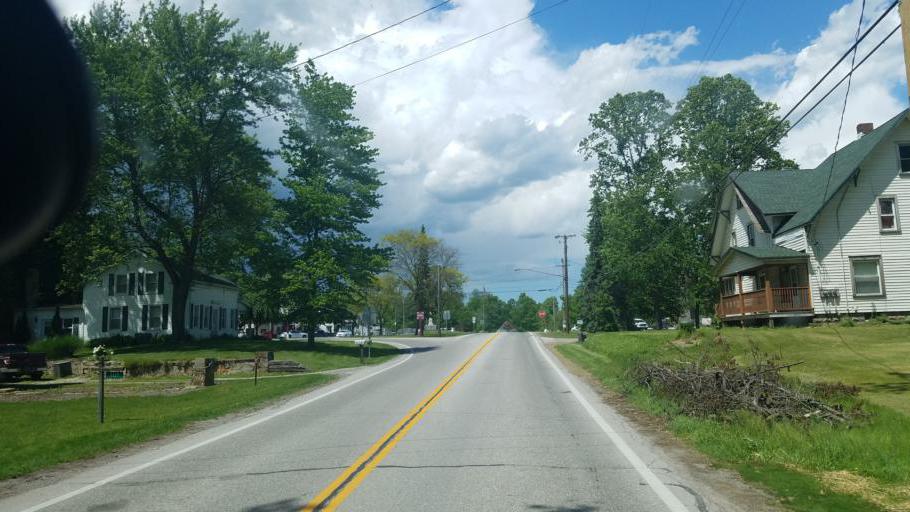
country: US
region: Ohio
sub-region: Ashtabula County
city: Orwell
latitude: 41.4573
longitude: -80.9547
